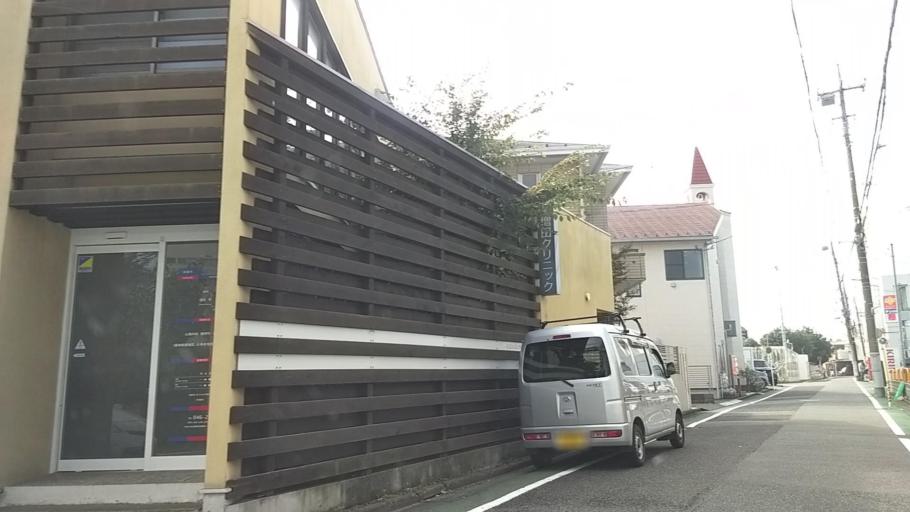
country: JP
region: Kanagawa
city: Atsugi
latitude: 35.4366
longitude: 139.3634
